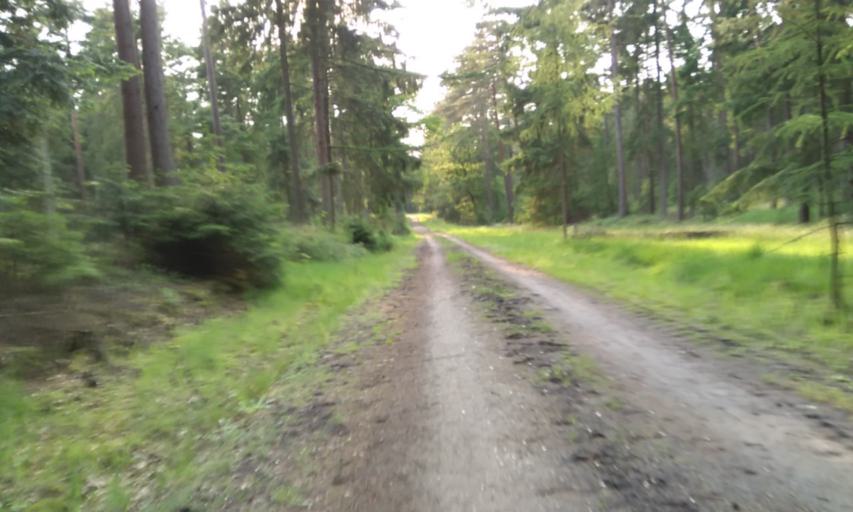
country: DE
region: Lower Saxony
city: Agathenburg
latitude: 53.5303
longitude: 9.5078
